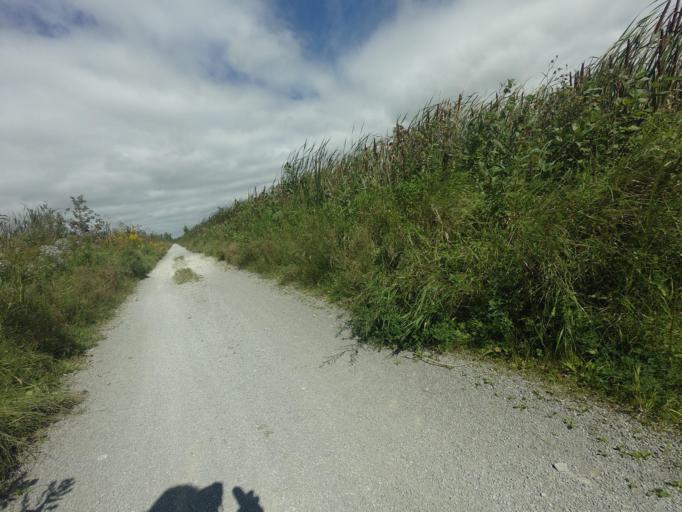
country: CA
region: Ontario
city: Uxbridge
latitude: 44.1882
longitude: -79.0669
